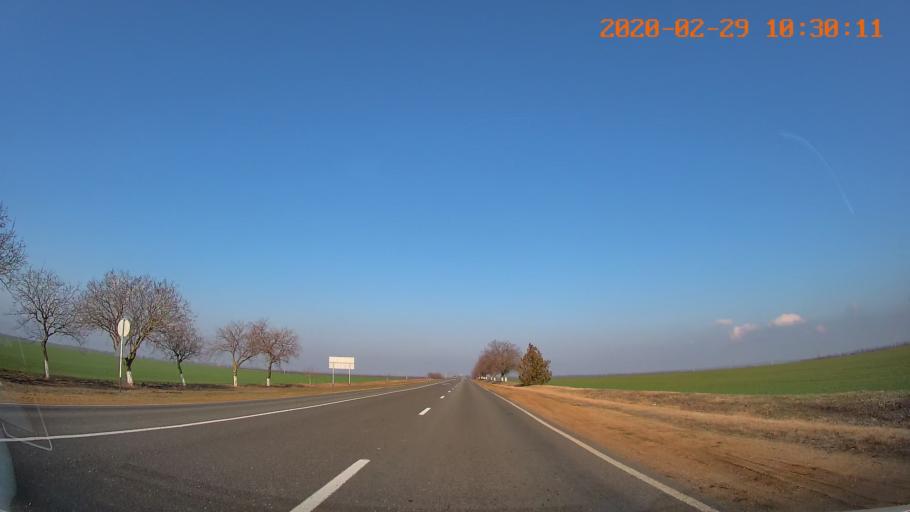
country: MD
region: Telenesti
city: Tiraspolul Nou
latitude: 46.9322
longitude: 29.5782
